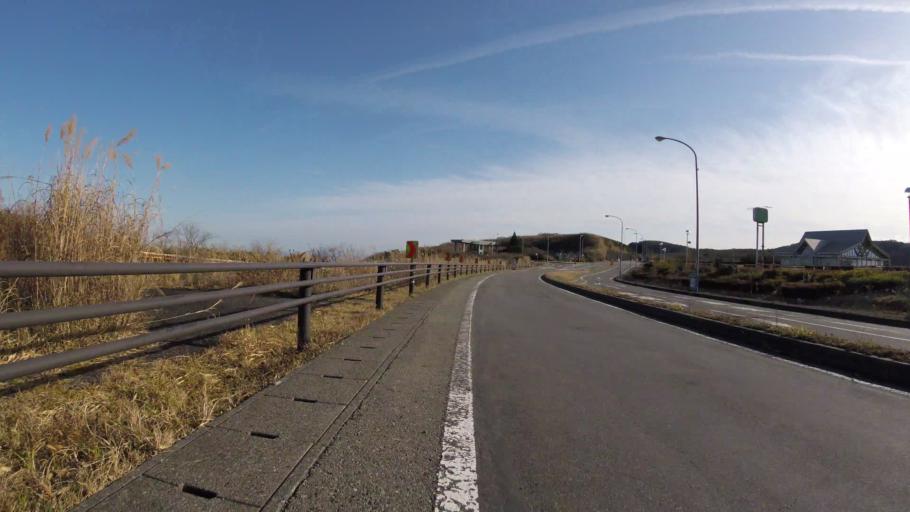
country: JP
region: Kanagawa
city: Hakone
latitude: 35.1680
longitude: 139.0282
